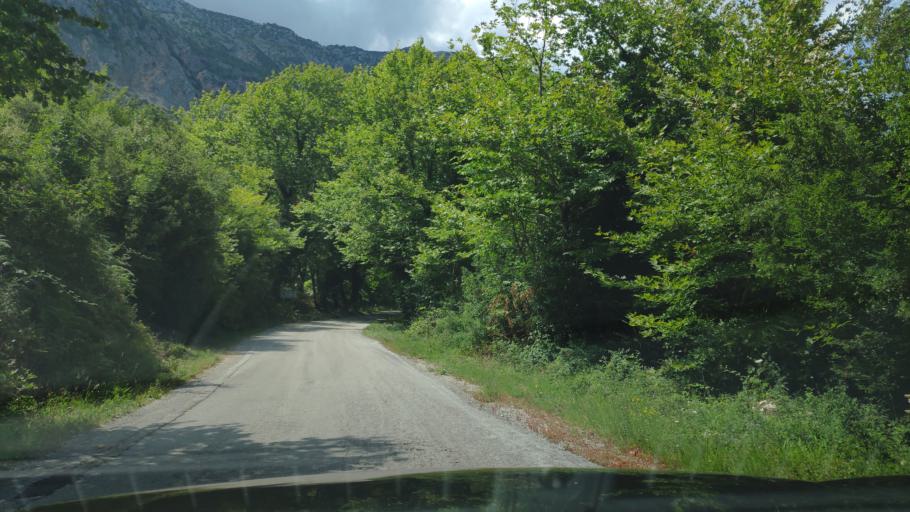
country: GR
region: Epirus
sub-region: Nomos Artas
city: Agios Dimitrios
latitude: 39.4355
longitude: 21.0153
